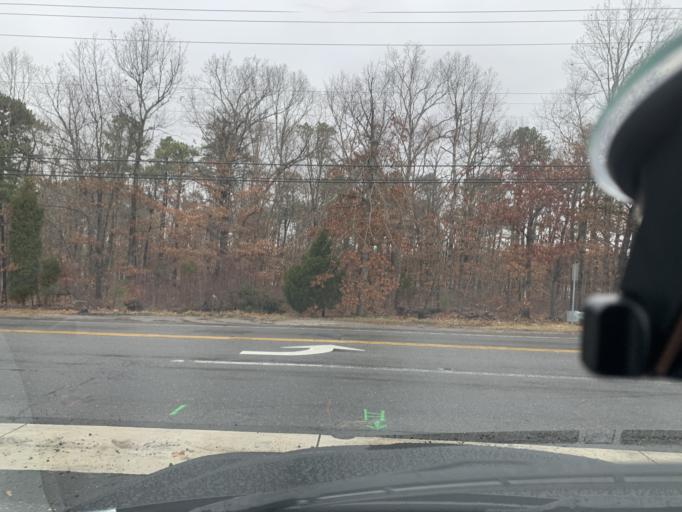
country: US
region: New Jersey
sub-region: Atlantic County
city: Pomona
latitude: 39.4350
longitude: -74.5921
